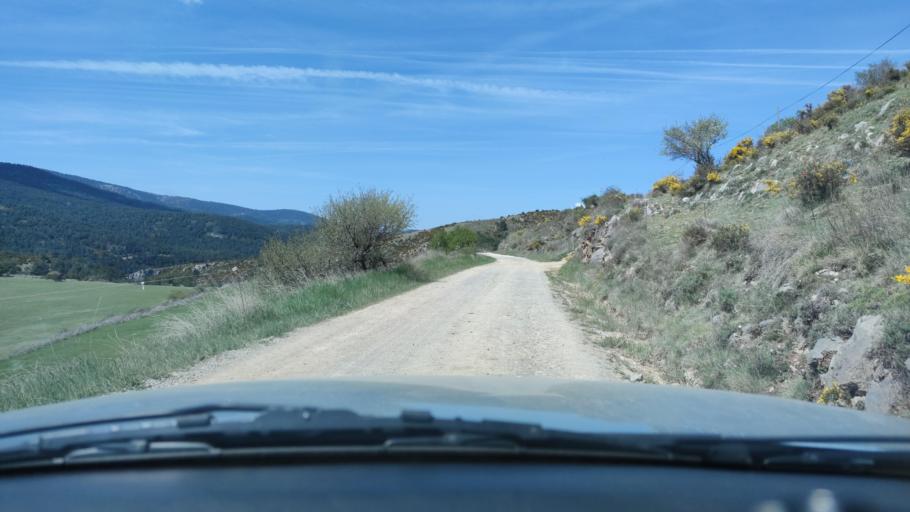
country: ES
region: Catalonia
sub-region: Provincia de Lleida
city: Sort
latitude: 42.2917
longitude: 1.1858
